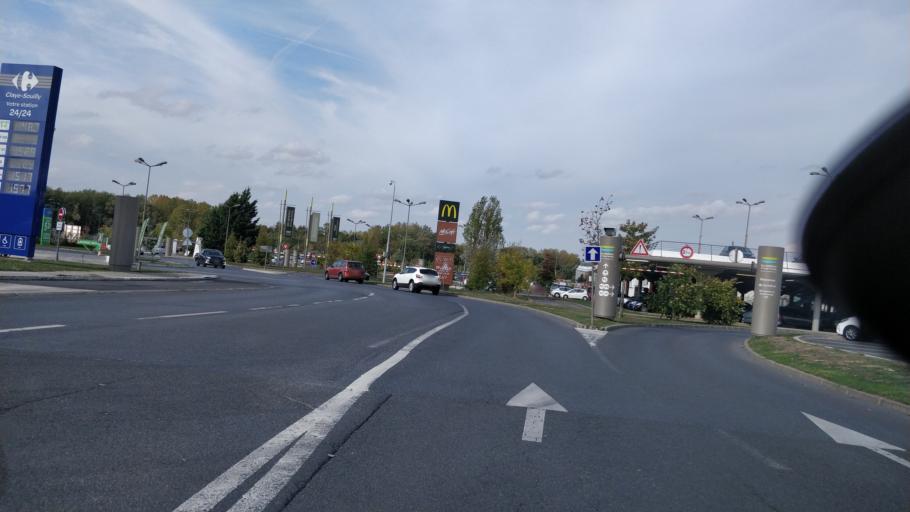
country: FR
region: Ile-de-France
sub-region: Departement de Seine-et-Marne
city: Claye-Souilly
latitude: 48.9446
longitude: 2.6610
